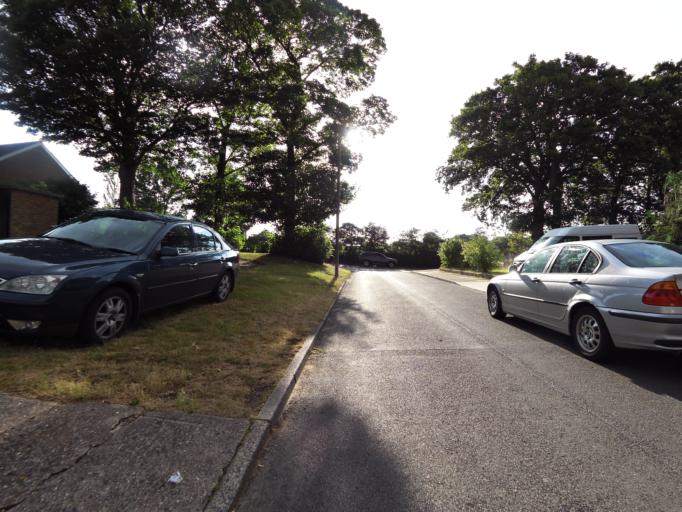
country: GB
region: England
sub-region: Suffolk
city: Ipswich
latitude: 52.0488
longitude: 1.1241
